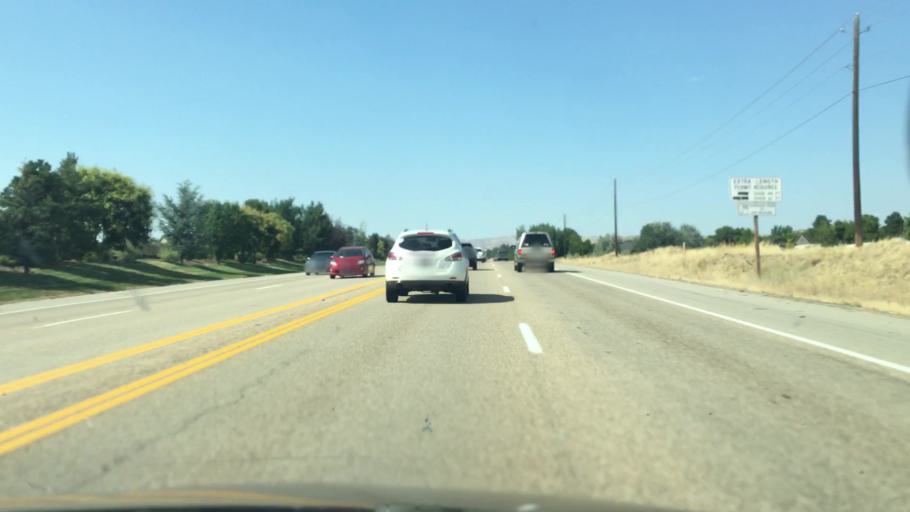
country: US
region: Idaho
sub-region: Ada County
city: Eagle
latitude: 43.6978
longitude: -116.3191
